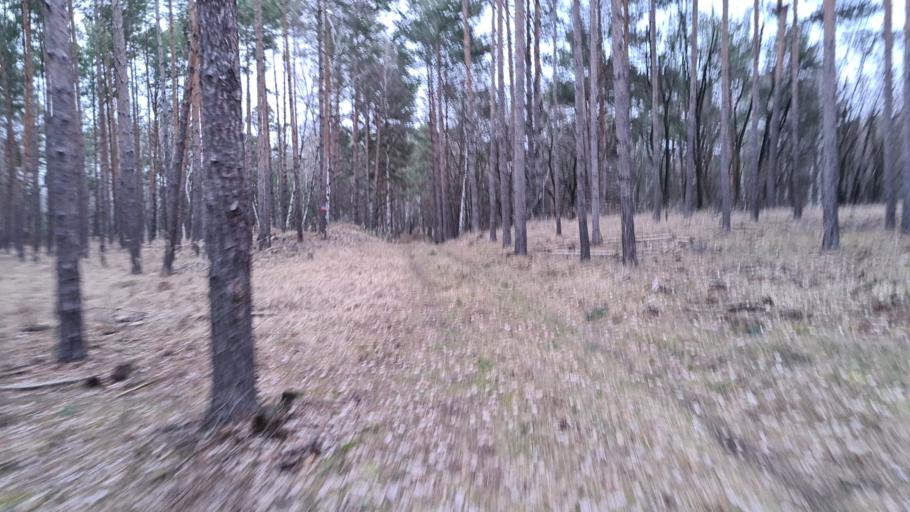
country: DE
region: Brandenburg
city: Trobitz
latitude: 51.5897
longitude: 13.4575
